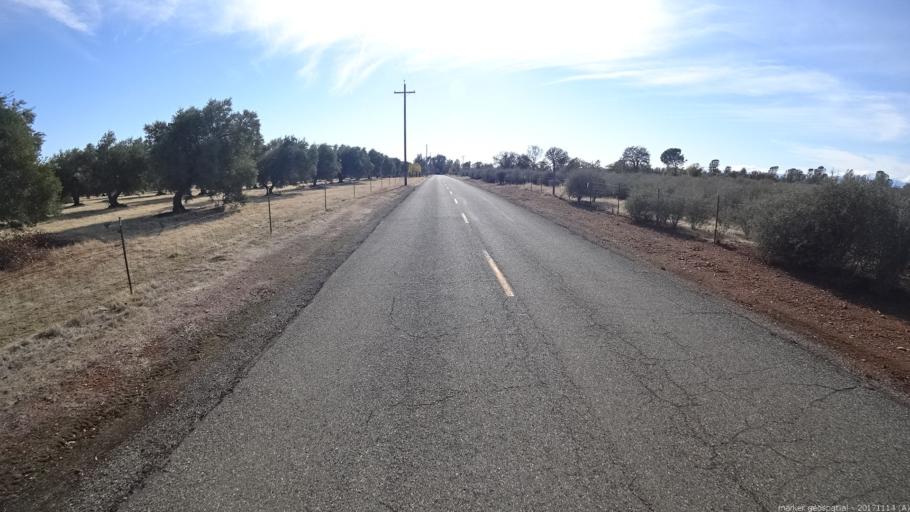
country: US
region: California
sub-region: Shasta County
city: Anderson
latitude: 40.4351
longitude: -122.4264
